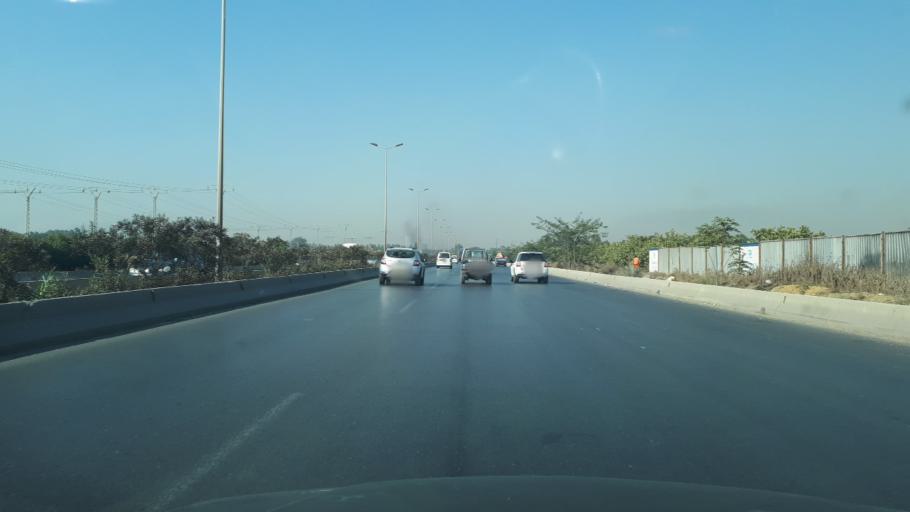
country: DZ
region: Tipaza
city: Baraki
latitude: 36.6907
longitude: 3.1213
